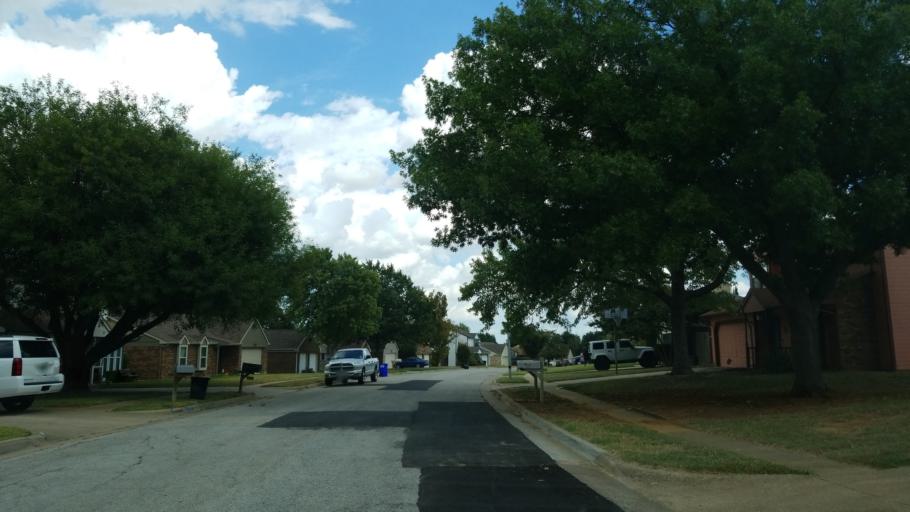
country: US
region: Texas
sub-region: Tarrant County
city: Euless
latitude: 32.8757
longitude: -97.0771
